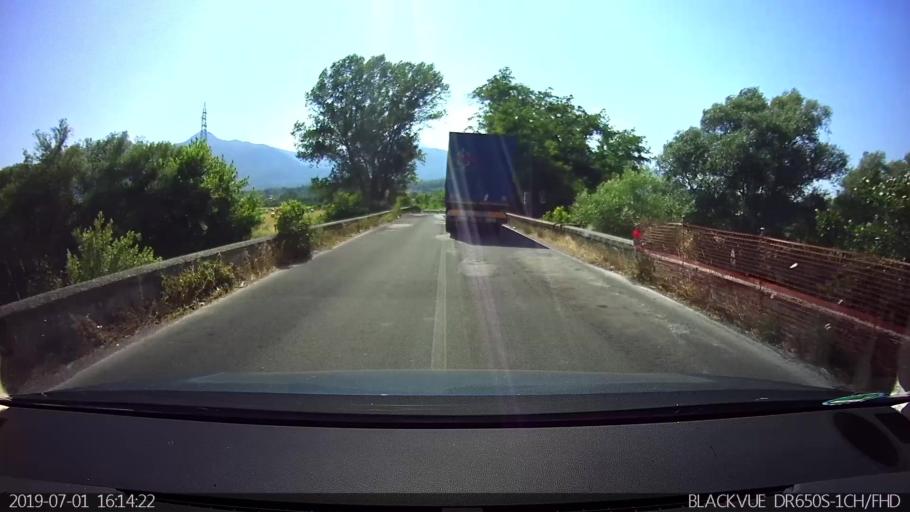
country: IT
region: Latium
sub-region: Provincia di Frosinone
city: Ceccano
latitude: 41.6010
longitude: 13.2970
